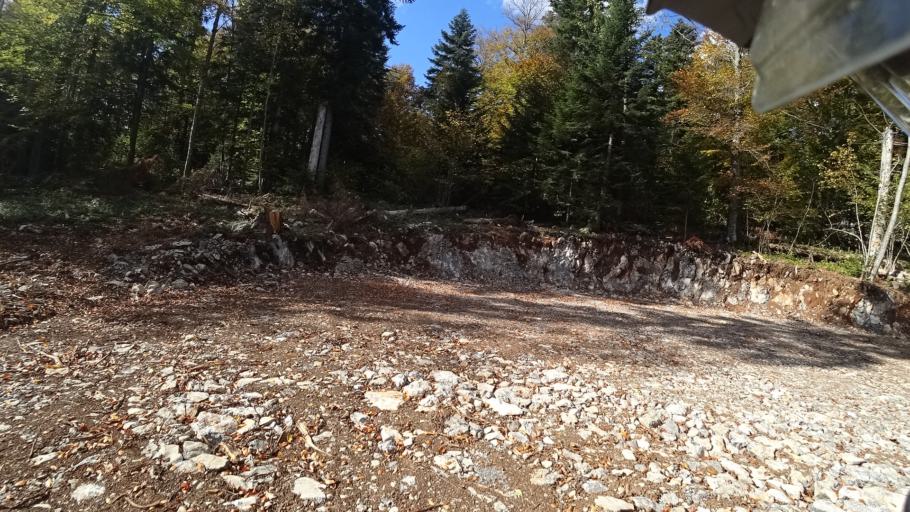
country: HR
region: Karlovacka
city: Plaski
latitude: 45.0575
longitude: 15.3551
